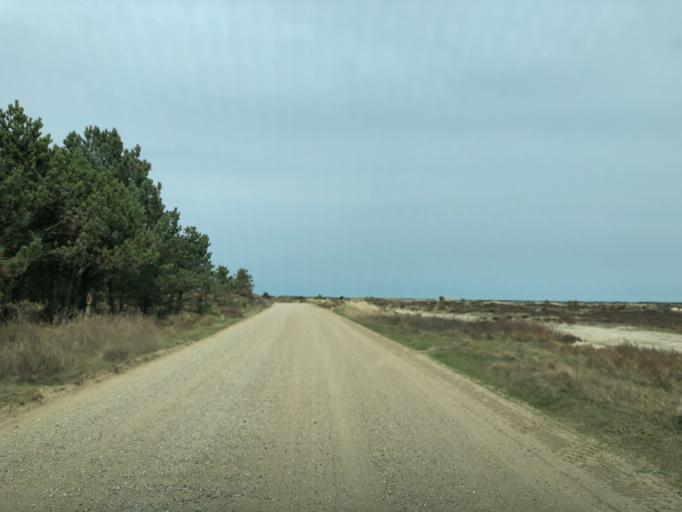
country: DK
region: South Denmark
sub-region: Varde Kommune
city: Oksbol
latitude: 55.5676
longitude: 8.1360
